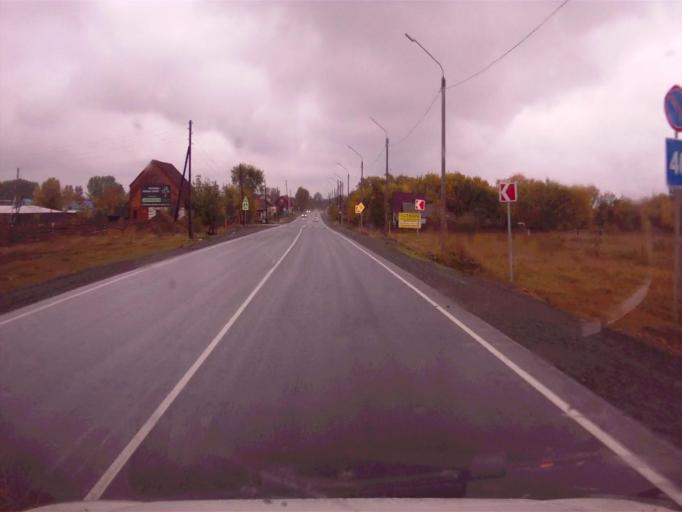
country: RU
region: Chelyabinsk
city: Novogornyy
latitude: 55.4970
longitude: 60.6528
